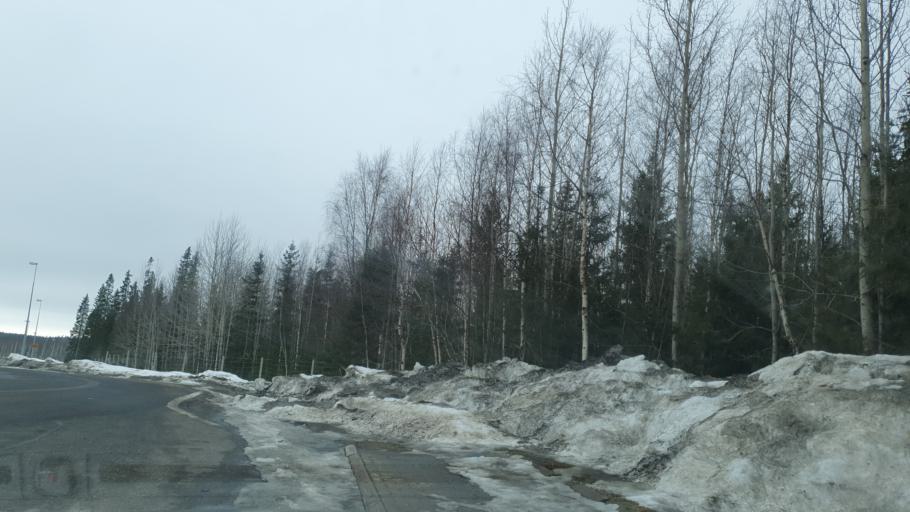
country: FI
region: Lapland
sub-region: Kemi-Tornio
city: Keminmaa
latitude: 65.8269
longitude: 24.4092
